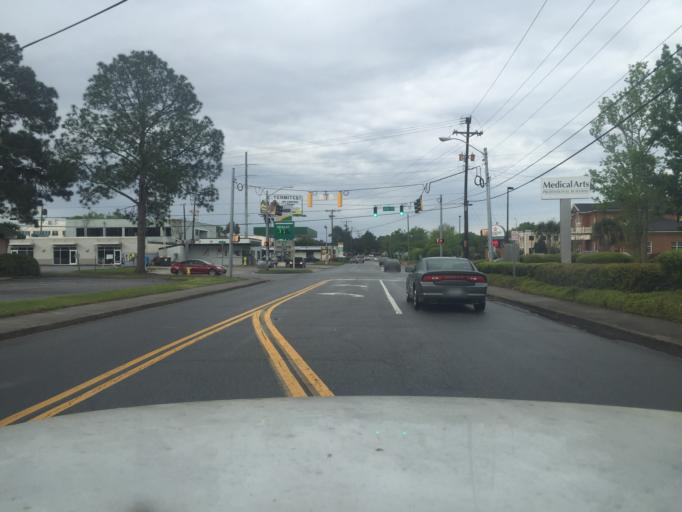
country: US
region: Georgia
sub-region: Chatham County
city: Thunderbolt
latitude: 32.0311
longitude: -81.0957
